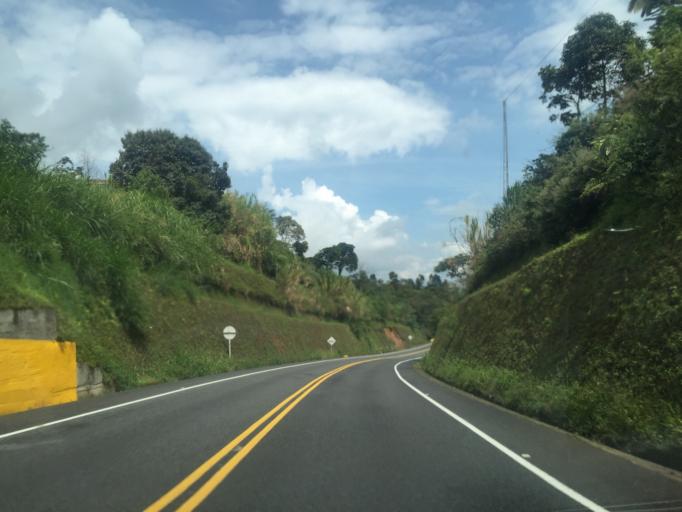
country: CO
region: Caldas
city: Chinchina
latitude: 4.9304
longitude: -75.6249
